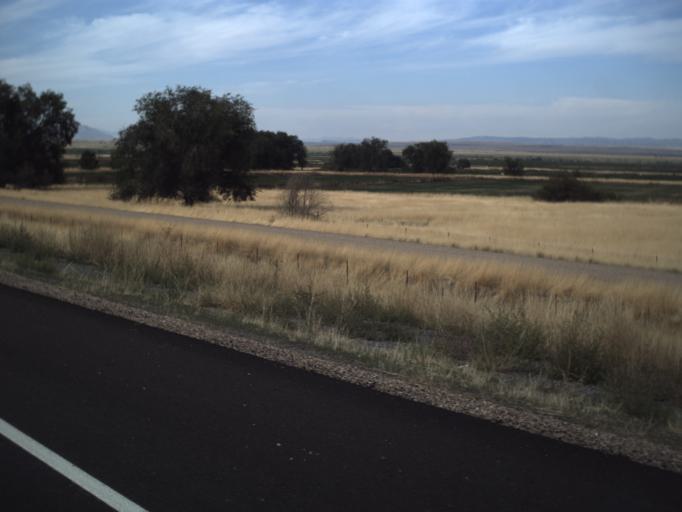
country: US
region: Utah
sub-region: Millard County
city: Fillmore
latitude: 38.8915
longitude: -112.4147
